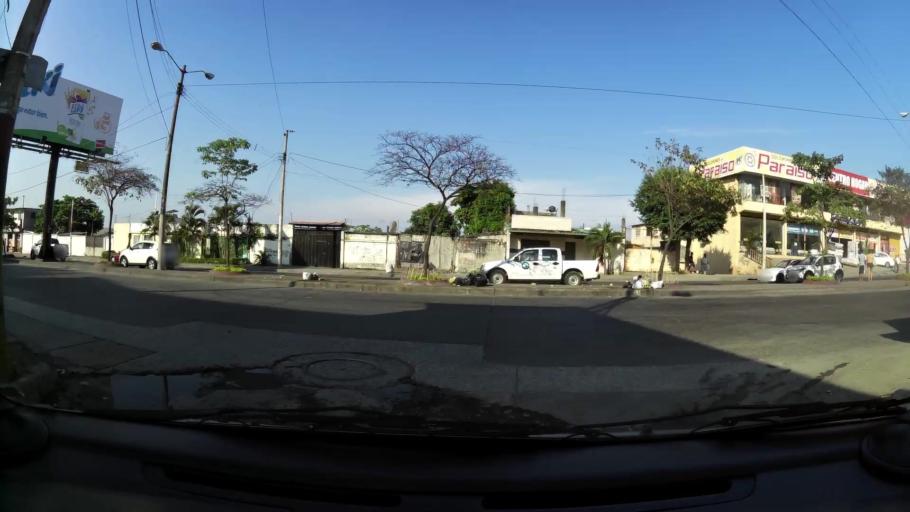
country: EC
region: Guayas
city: Guayaquil
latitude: -2.1536
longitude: -79.9134
